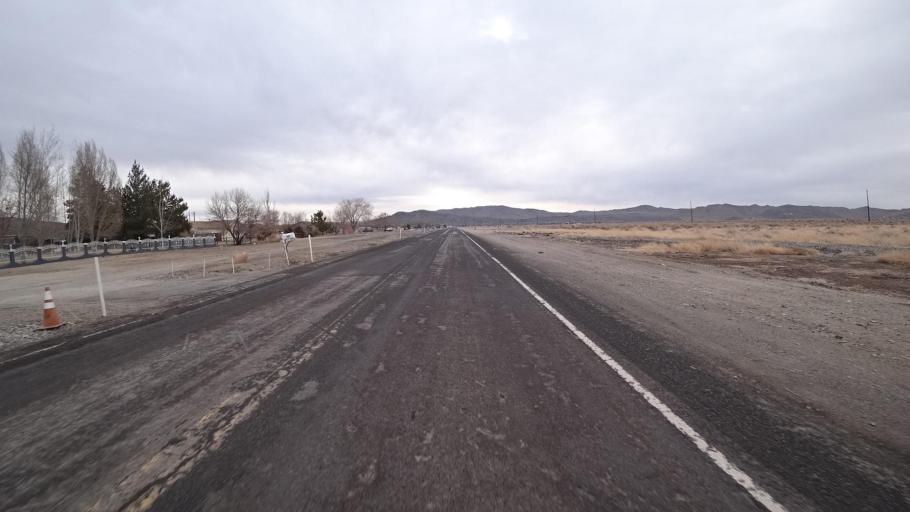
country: US
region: Nevada
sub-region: Washoe County
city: Lemmon Valley
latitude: 39.6738
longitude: -119.8422
